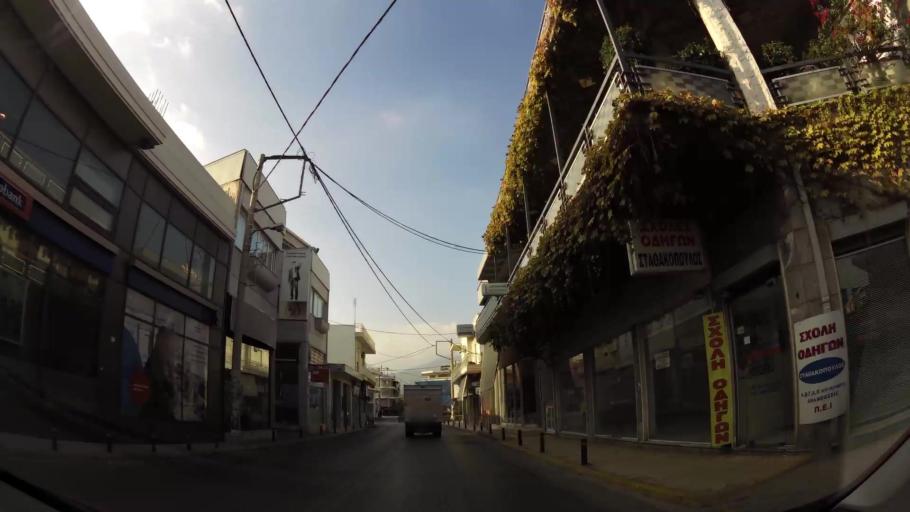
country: GR
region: Attica
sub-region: Nomarchia Anatolikis Attikis
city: Acharnes
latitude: 38.0782
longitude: 23.7384
